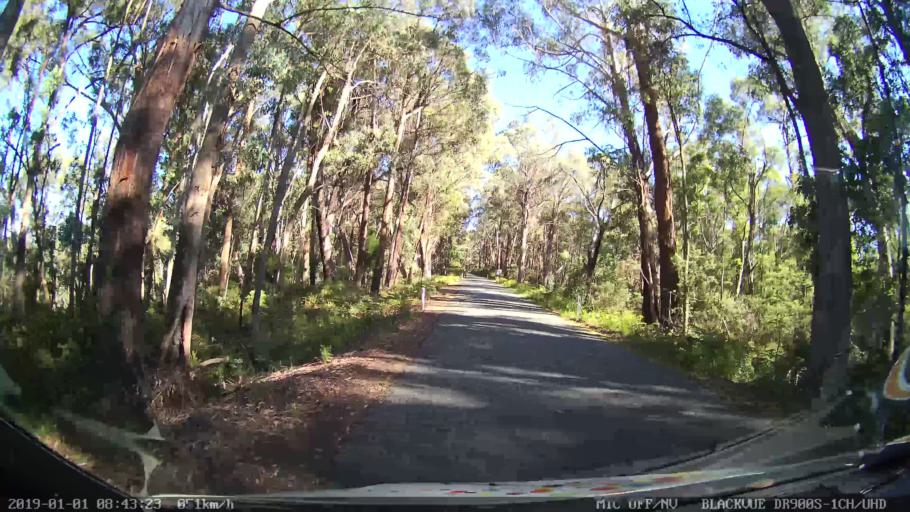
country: AU
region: New South Wales
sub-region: Snowy River
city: Jindabyne
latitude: -36.3177
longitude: 148.1932
